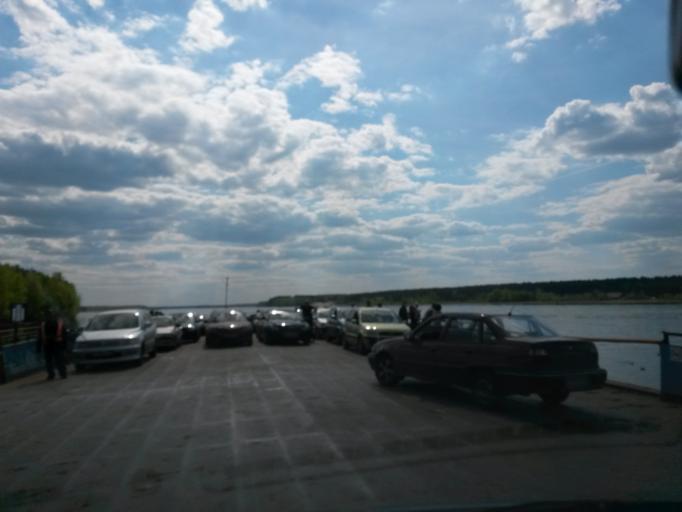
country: RU
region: Jaroslavl
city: Myshkin
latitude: 57.7764
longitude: 38.4592
